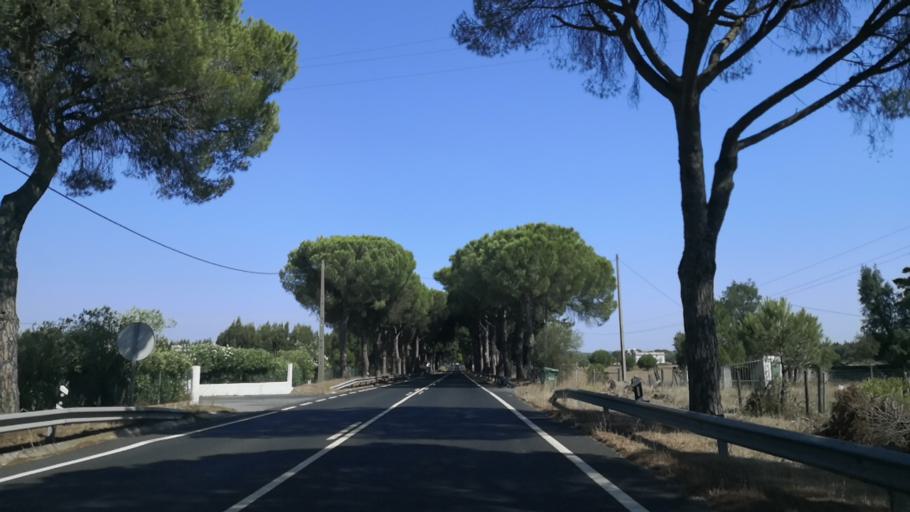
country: PT
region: Evora
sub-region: Vendas Novas
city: Vendas Novas
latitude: 38.7219
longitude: -8.6349
